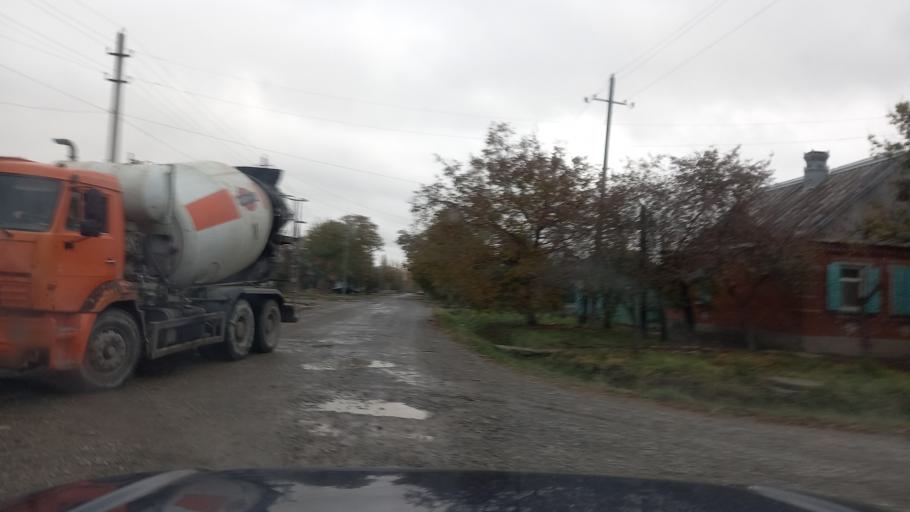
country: RU
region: Adygeya
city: Maykop
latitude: 44.6170
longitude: 40.1284
